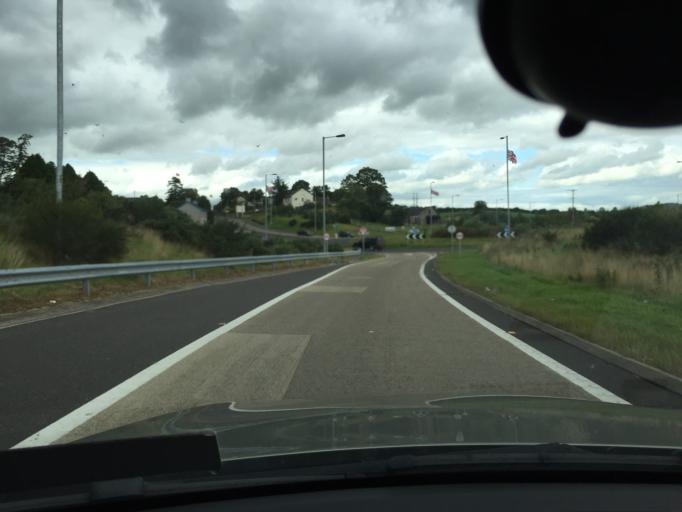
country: GB
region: Northern Ireland
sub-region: Newry and Mourne District
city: Newry
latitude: 54.1993
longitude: -6.3618
